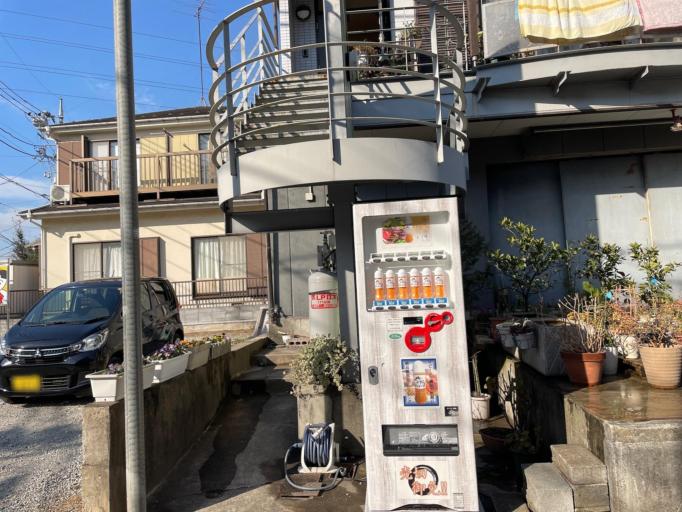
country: JP
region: Saitama
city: Wako
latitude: 35.7949
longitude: 139.6303
